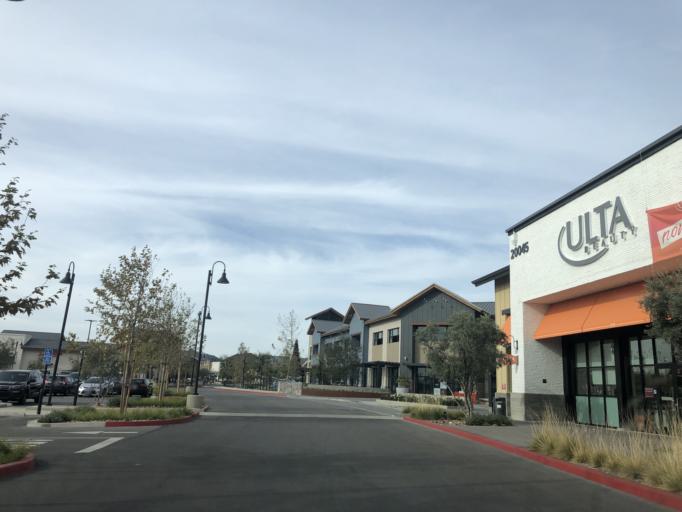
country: US
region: California
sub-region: Los Angeles County
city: Chatsworth
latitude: 34.2768
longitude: -118.5714
